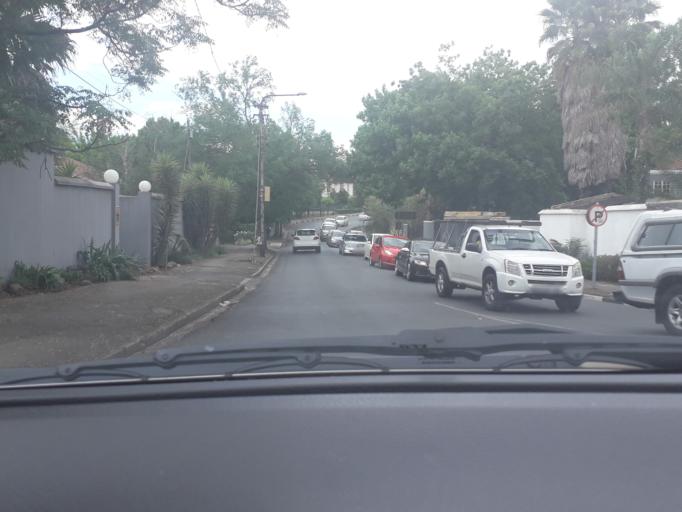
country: ZA
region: Gauteng
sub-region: City of Johannesburg Metropolitan Municipality
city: Johannesburg
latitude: -26.1515
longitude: 28.0225
